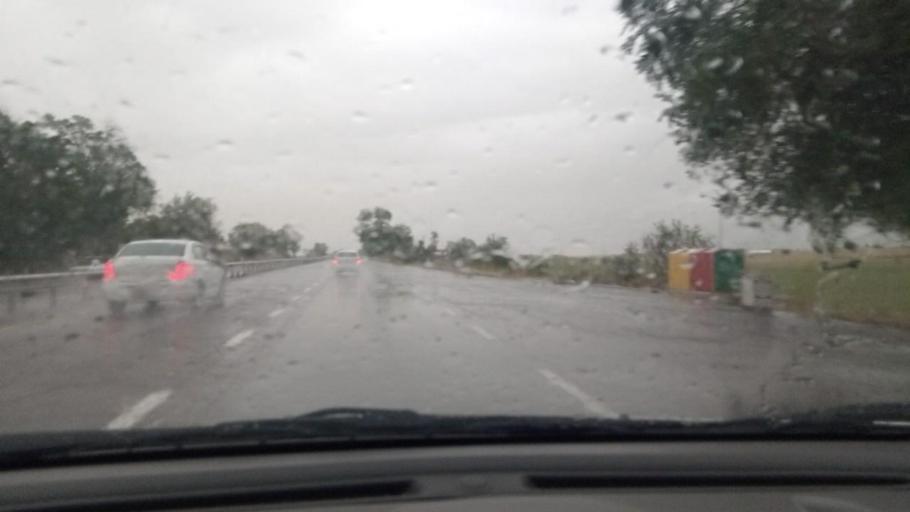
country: UZ
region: Toshkent
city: Ohangaron
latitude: 40.9960
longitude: 69.5292
